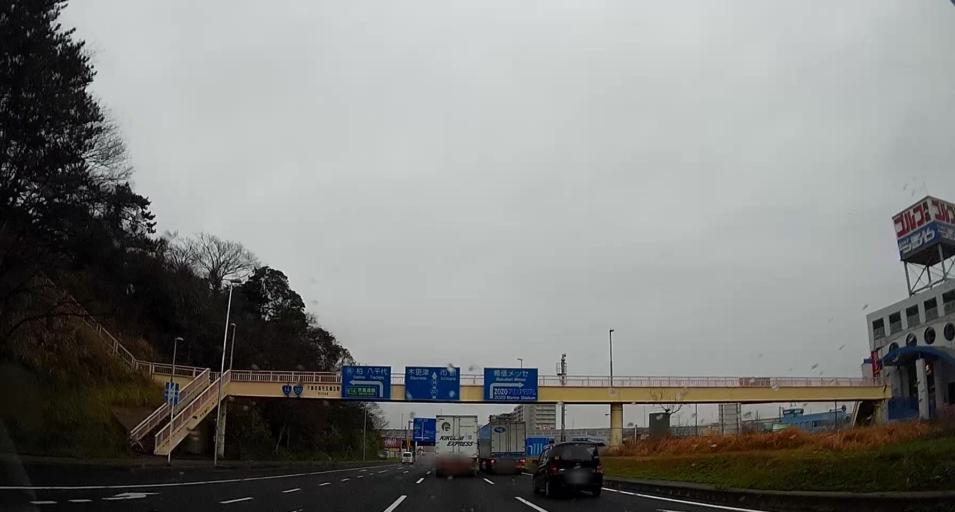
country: JP
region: Chiba
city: Chiba
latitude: 35.6292
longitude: 140.0880
